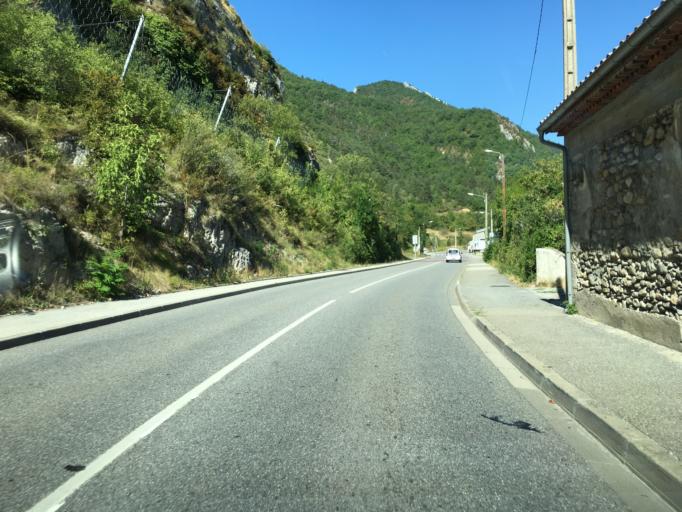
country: FR
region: Provence-Alpes-Cote d'Azur
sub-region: Departement des Hautes-Alpes
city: Serres
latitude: 44.4306
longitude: 5.7153
